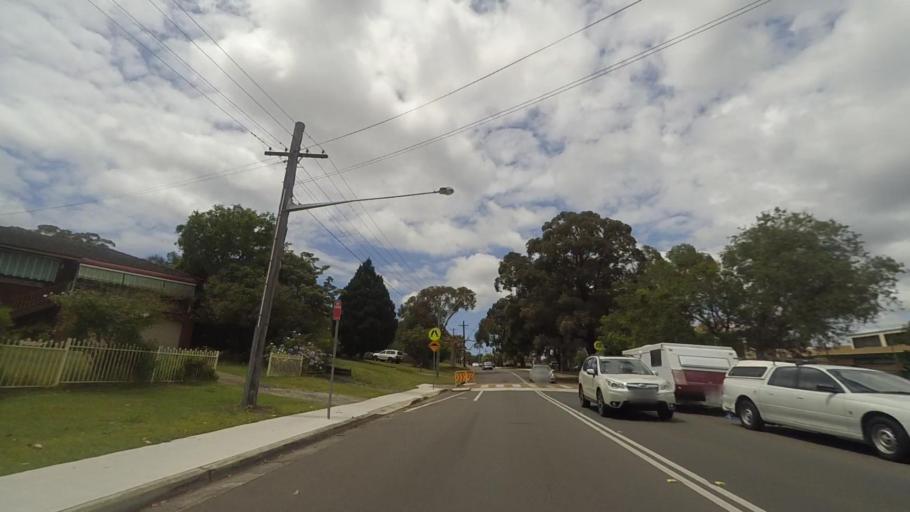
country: AU
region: New South Wales
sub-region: Sutherland Shire
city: Engadine
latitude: -34.0726
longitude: 151.0099
